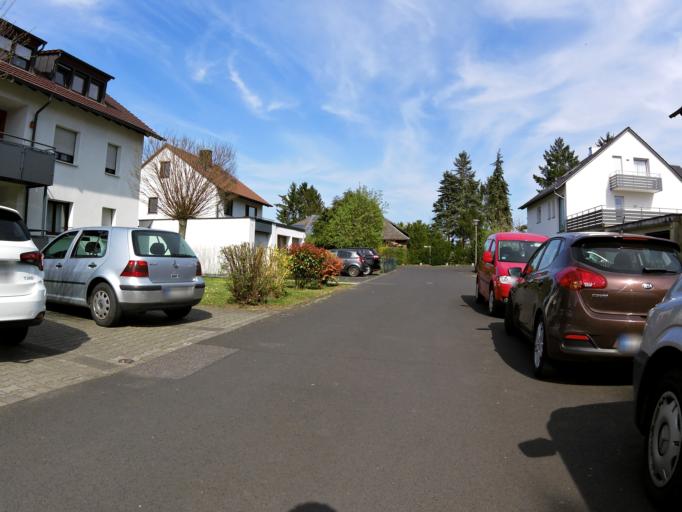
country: DE
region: Bavaria
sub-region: Regierungsbezirk Unterfranken
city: Unterpleichfeld
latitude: 49.8726
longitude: 10.0346
